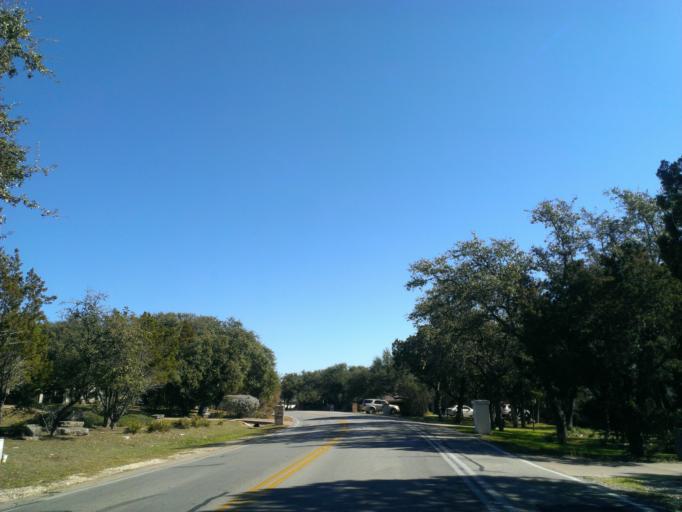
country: US
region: Texas
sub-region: Travis County
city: Lakeway
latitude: 30.3683
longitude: -97.9794
